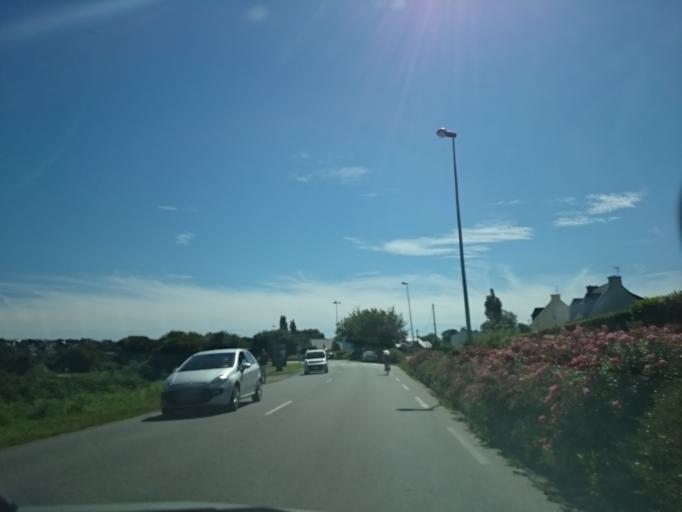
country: FR
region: Brittany
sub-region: Departement du Finistere
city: Saint-Renan
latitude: 48.4366
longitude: -4.6284
